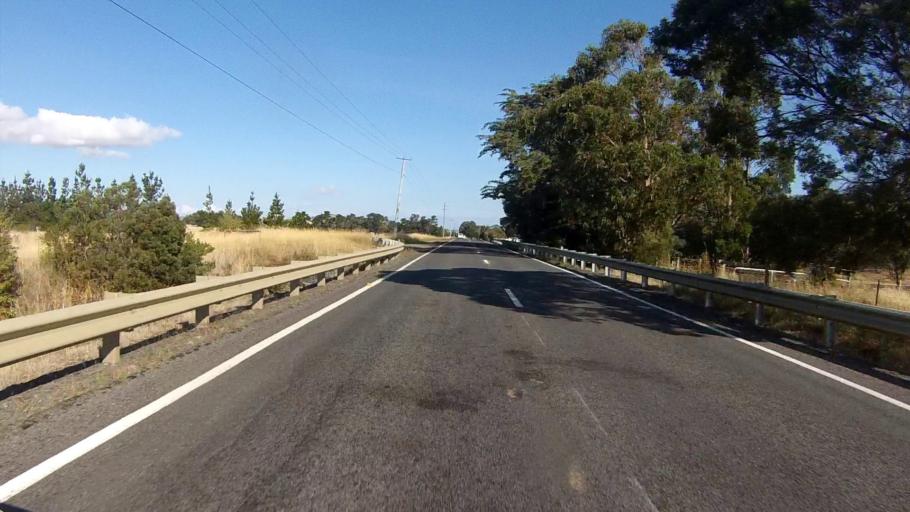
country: AU
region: Tasmania
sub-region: Sorell
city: Sorell
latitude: -42.7239
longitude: 147.5215
